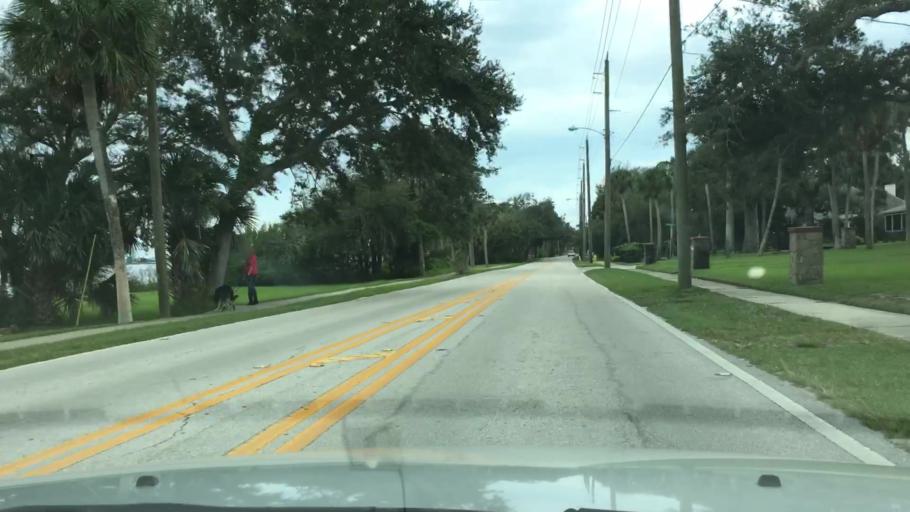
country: US
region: Florida
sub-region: Volusia County
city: Ormond Beach
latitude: 29.2832
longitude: -81.0545
